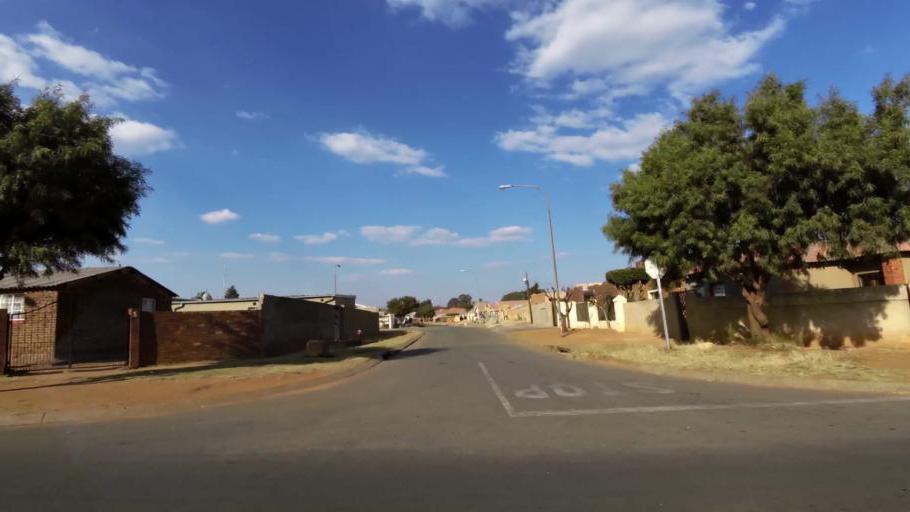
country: ZA
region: Gauteng
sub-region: City of Johannesburg Metropolitan Municipality
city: Roodepoort
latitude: -26.2099
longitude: 27.8772
